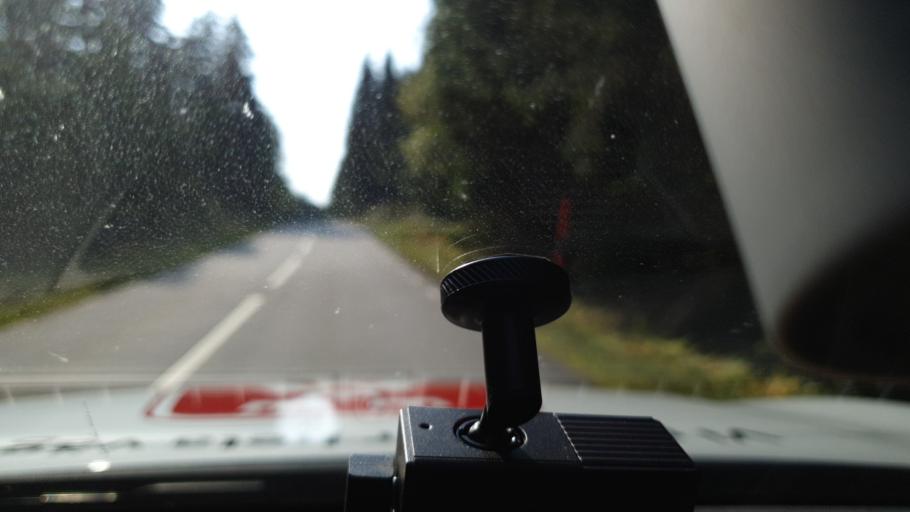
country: SE
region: Kalmar
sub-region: Vasterviks Kommun
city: Overum
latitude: 57.9059
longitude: 16.1032
